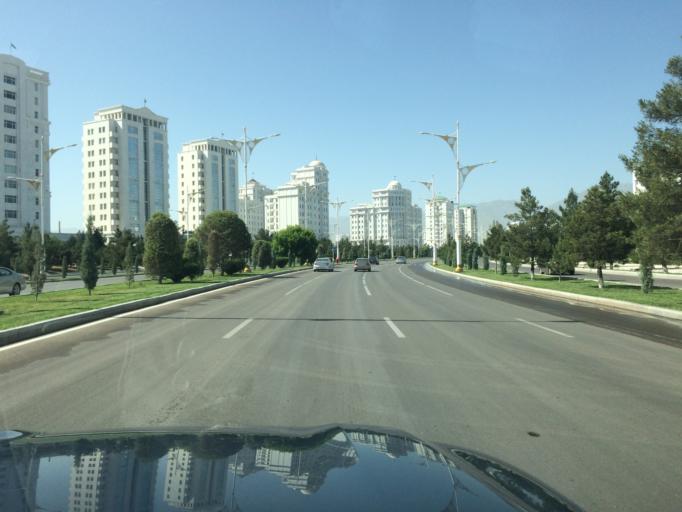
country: TM
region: Ahal
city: Ashgabat
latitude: 37.9051
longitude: 58.3654
